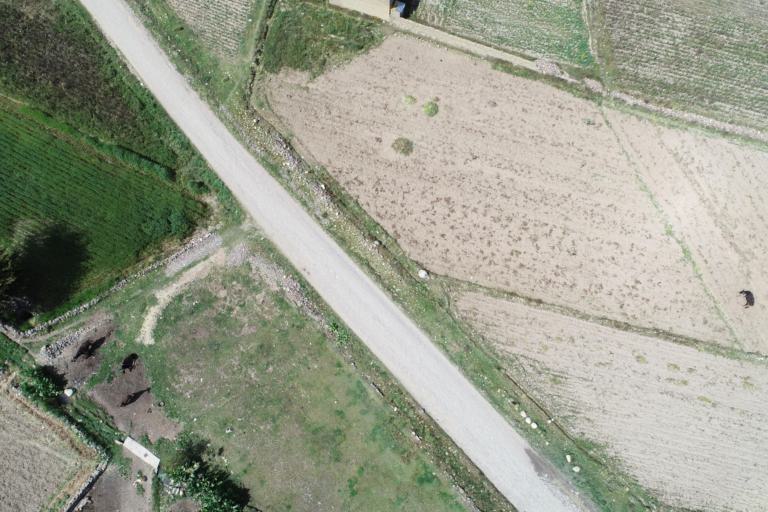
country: BO
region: La Paz
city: Achacachi
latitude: -16.0214
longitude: -68.6159
